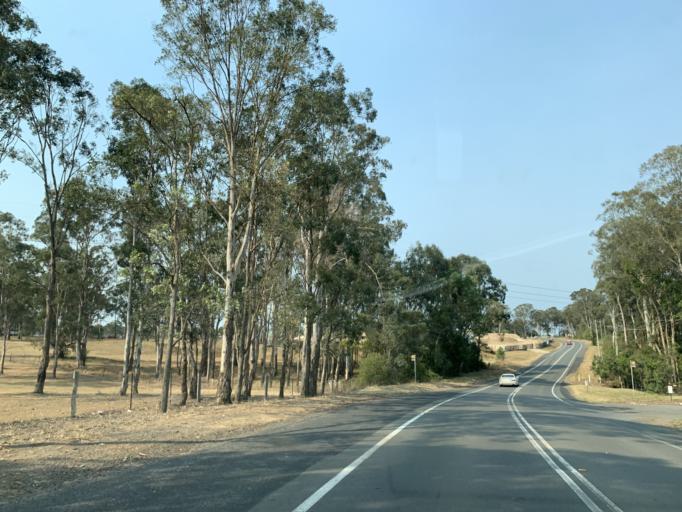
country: AU
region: New South Wales
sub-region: Blacktown
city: Rouse Hill
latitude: -33.6635
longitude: 150.9203
